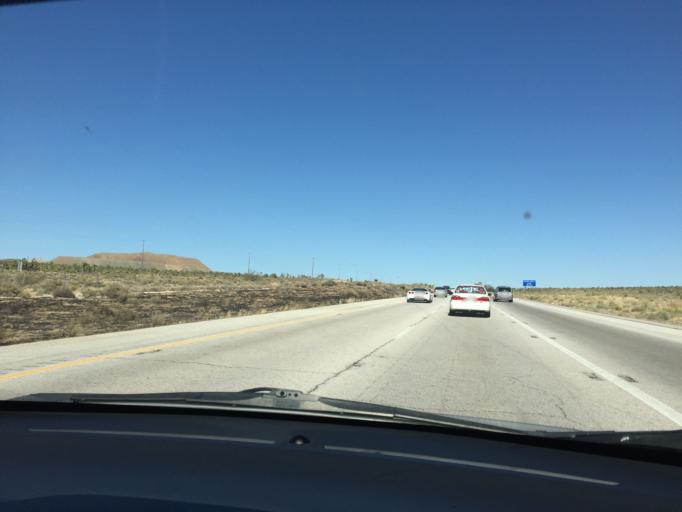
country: US
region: Nevada
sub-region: Clark County
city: Sandy Valley
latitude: 35.4717
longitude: -115.5600
